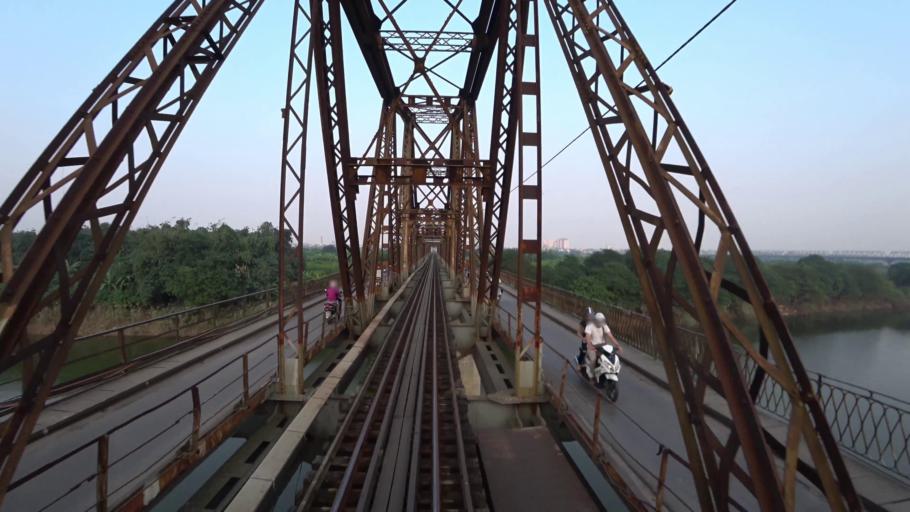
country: VN
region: Ha Noi
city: Hoan Kiem
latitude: 21.0433
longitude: 105.8585
